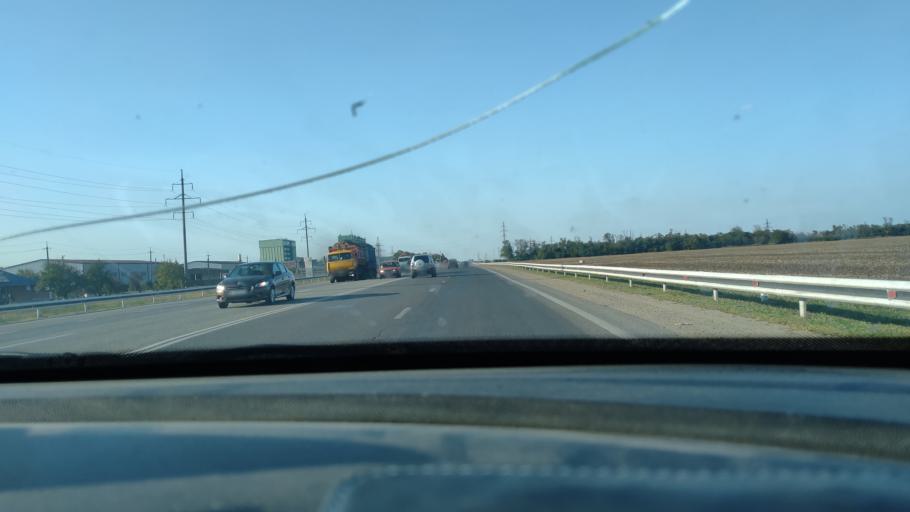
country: RU
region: Krasnodarskiy
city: Timashevsk
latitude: 45.6119
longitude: 38.9875
